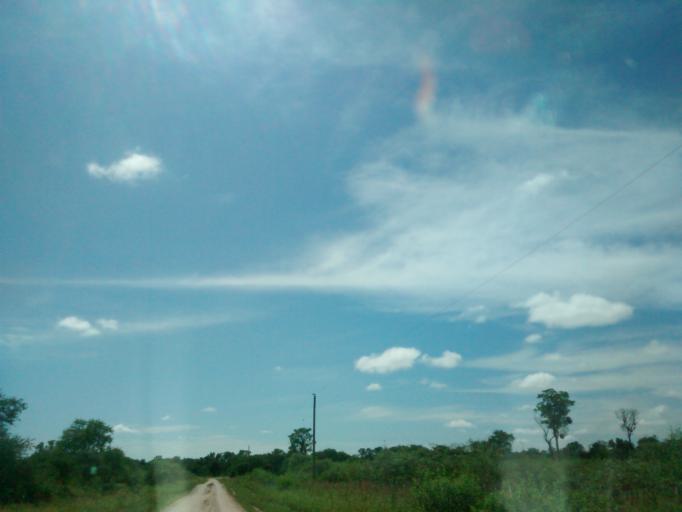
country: AR
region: Chaco
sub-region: Departamento de Quitilipi
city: Quitilipi
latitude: -26.7927
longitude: -60.1972
